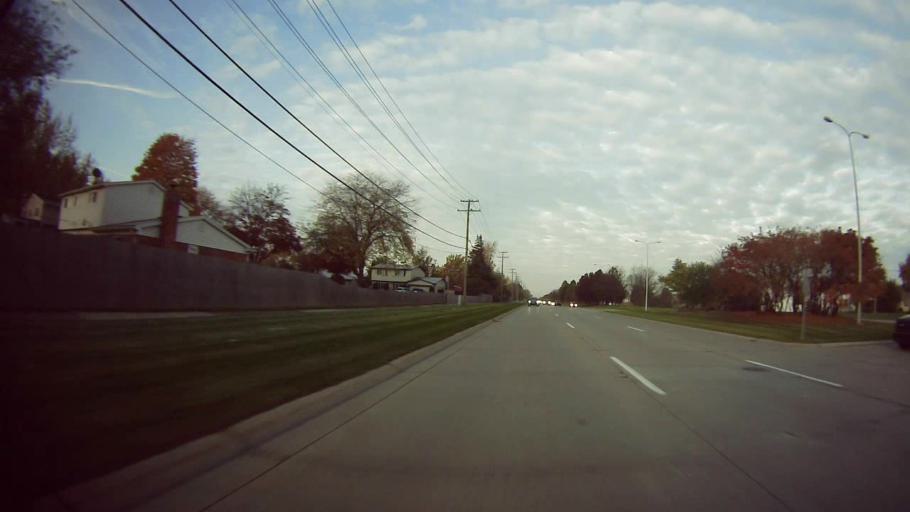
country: US
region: Michigan
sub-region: Macomb County
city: Sterling Heights
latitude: 42.5648
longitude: -83.0571
